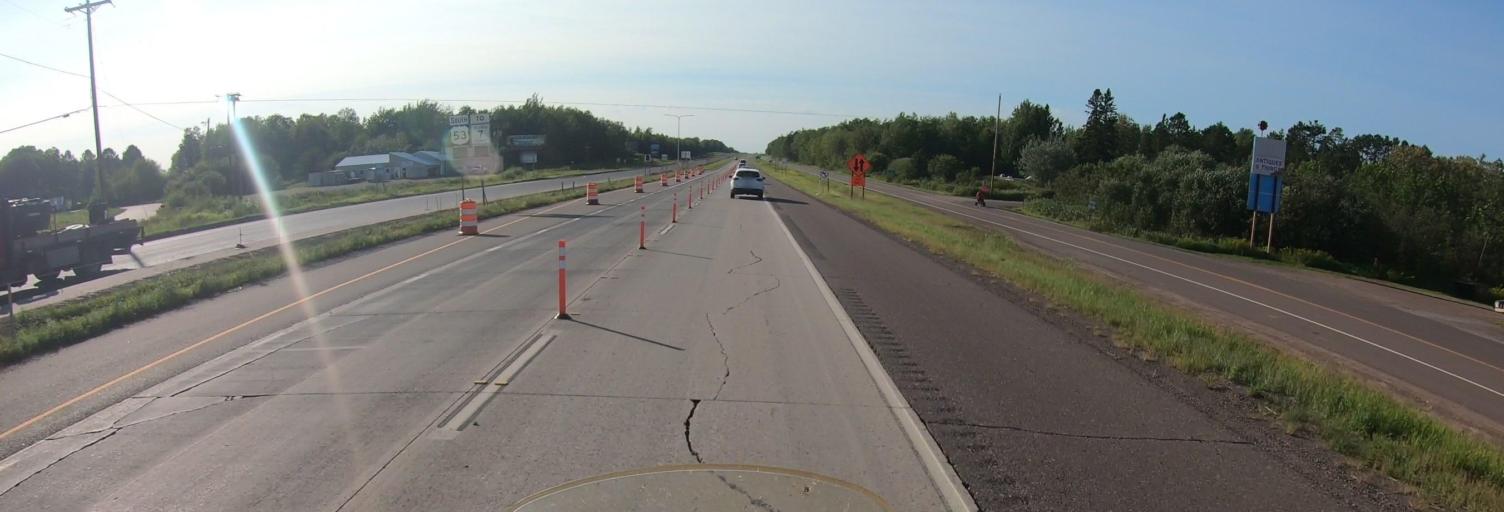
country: US
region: Minnesota
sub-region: Saint Louis County
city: Hermantown
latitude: 46.8946
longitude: -92.3644
